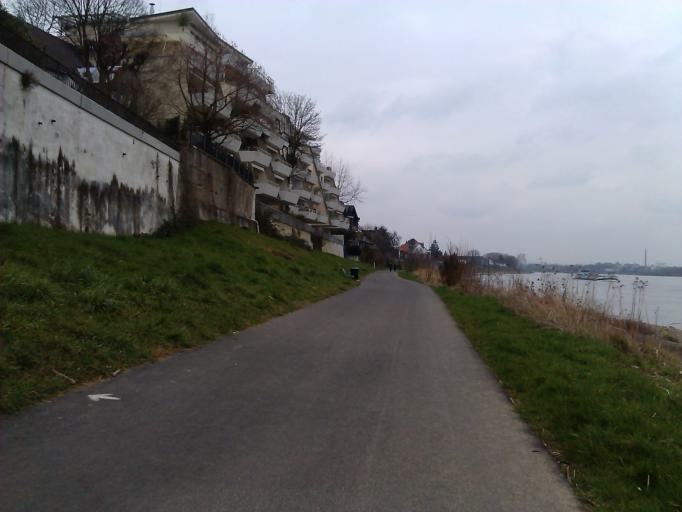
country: DE
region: North Rhine-Westphalia
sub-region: Regierungsbezirk Koln
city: Porz am Rhein
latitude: 50.8688
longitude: 7.0224
